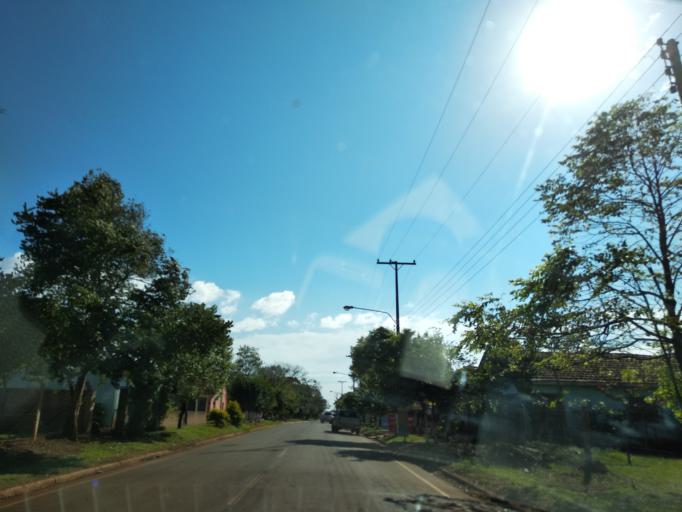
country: PY
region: Itapua
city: Hohenau
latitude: -27.0574
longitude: -55.7406
